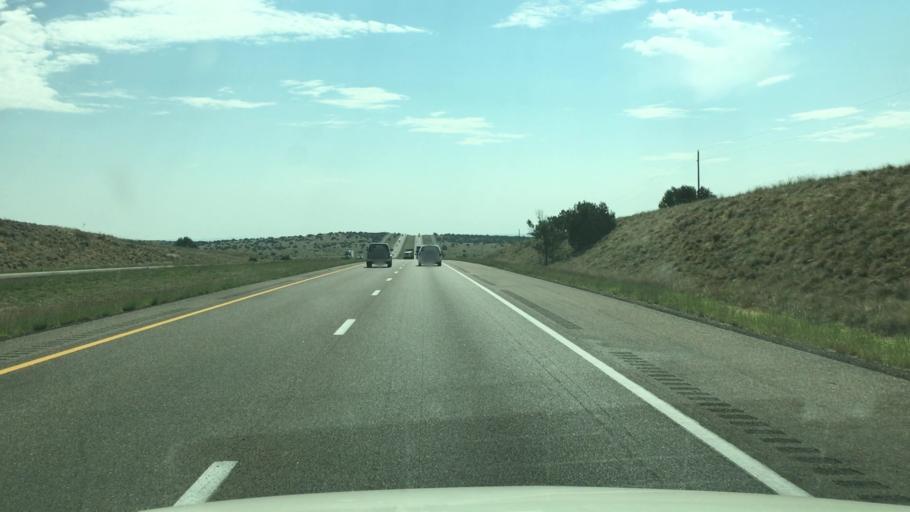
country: US
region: New Mexico
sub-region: Guadalupe County
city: Santa Rosa
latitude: 34.9722
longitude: -104.9101
